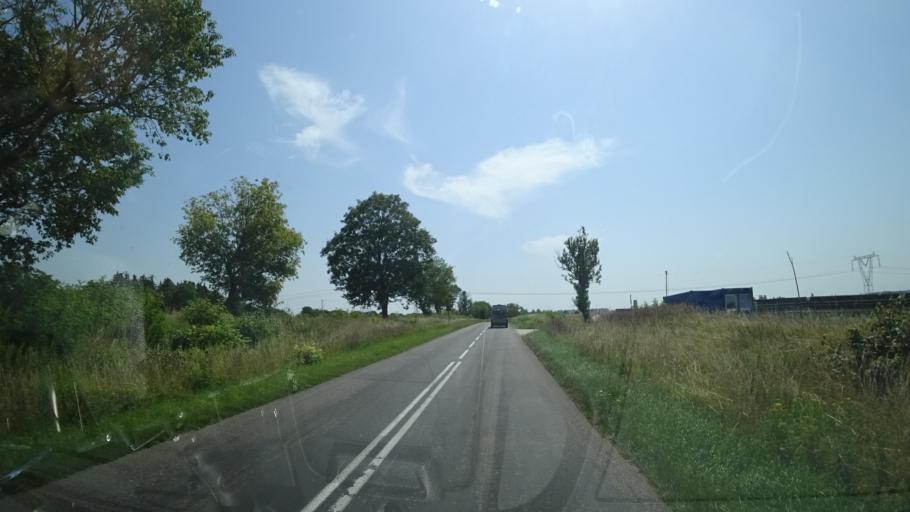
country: PL
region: West Pomeranian Voivodeship
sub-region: Powiat lobeski
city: Lobez
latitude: 53.7318
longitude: 15.5767
